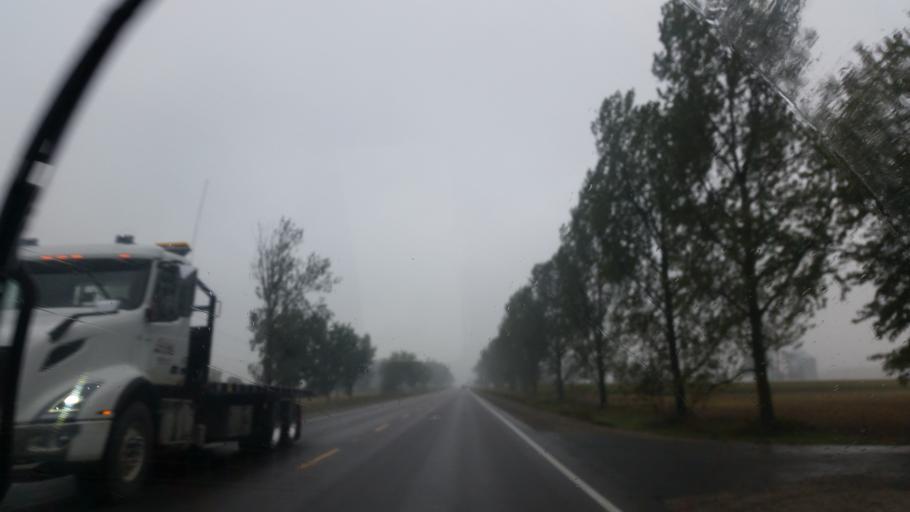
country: CA
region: Ontario
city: Stratford
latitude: 43.3317
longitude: -81.0164
